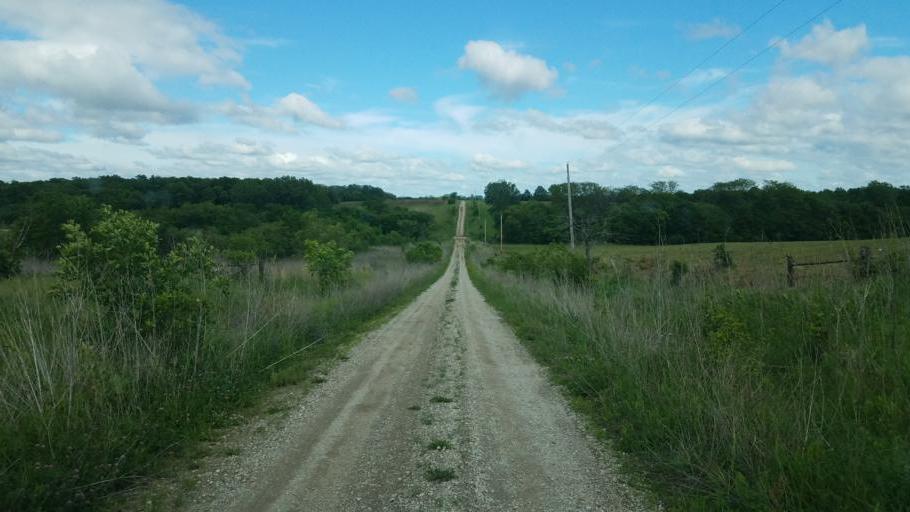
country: US
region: Missouri
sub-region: Mercer County
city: Princeton
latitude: 40.2601
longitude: -93.6988
